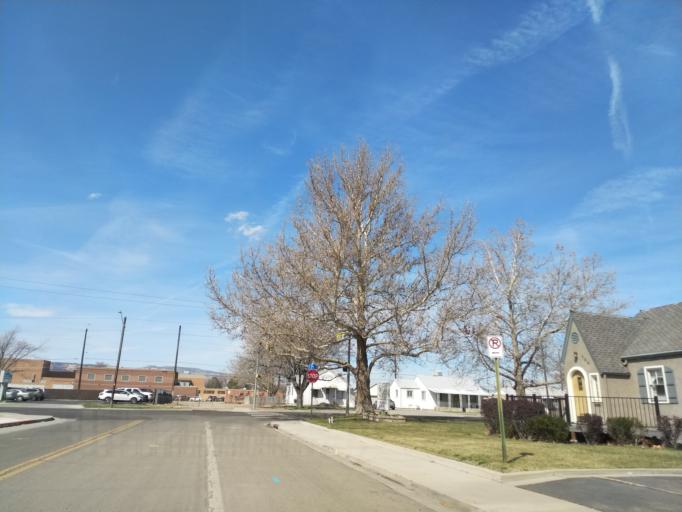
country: US
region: Colorado
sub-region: Mesa County
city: Grand Junction
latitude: 39.0810
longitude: -108.5605
